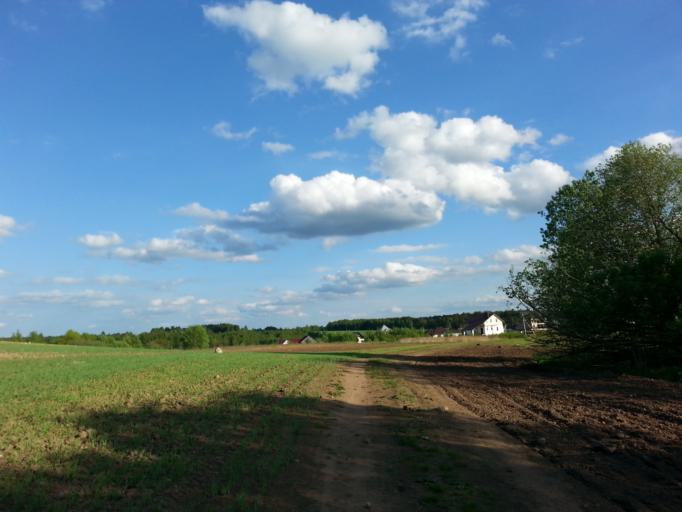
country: BY
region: Minsk
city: Narach
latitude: 54.9391
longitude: 26.7025
